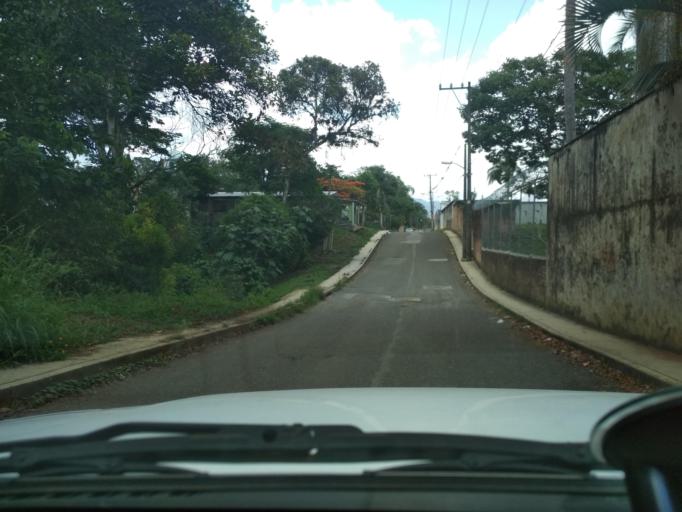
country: MX
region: Veracruz
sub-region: Cordoba
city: San Jose de Abajo [Unidad Habitacional]
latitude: 18.9160
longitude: -96.9562
